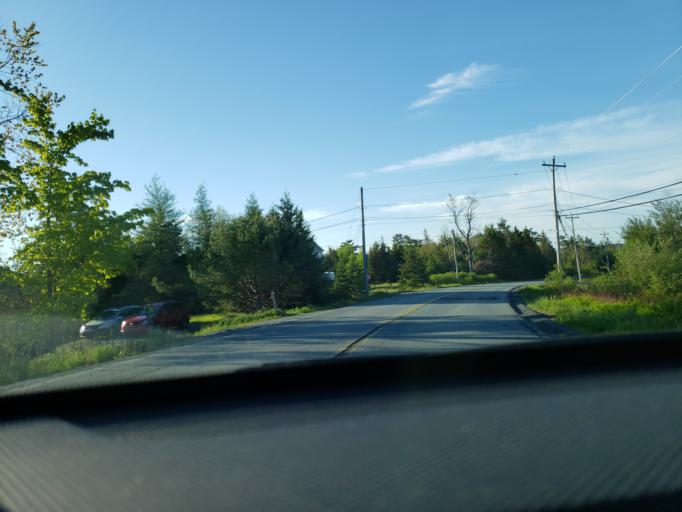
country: CA
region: Nova Scotia
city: Cole Harbour
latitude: 44.7196
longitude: -63.3978
